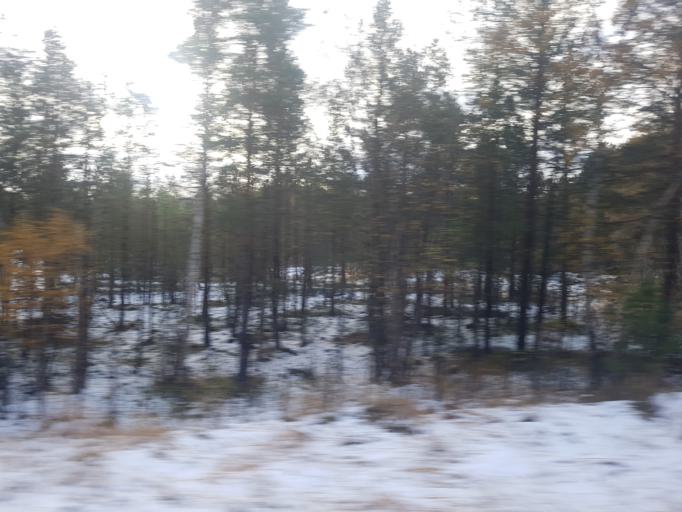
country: NO
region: Sor-Trondelag
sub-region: Oppdal
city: Oppdal
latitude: 62.6327
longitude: 9.7934
